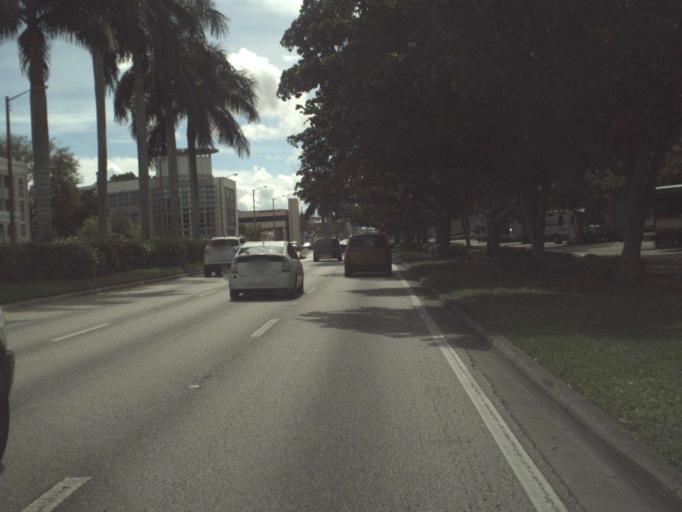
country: US
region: Florida
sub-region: Miami-Dade County
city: South Miami
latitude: 25.7116
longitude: -80.2807
